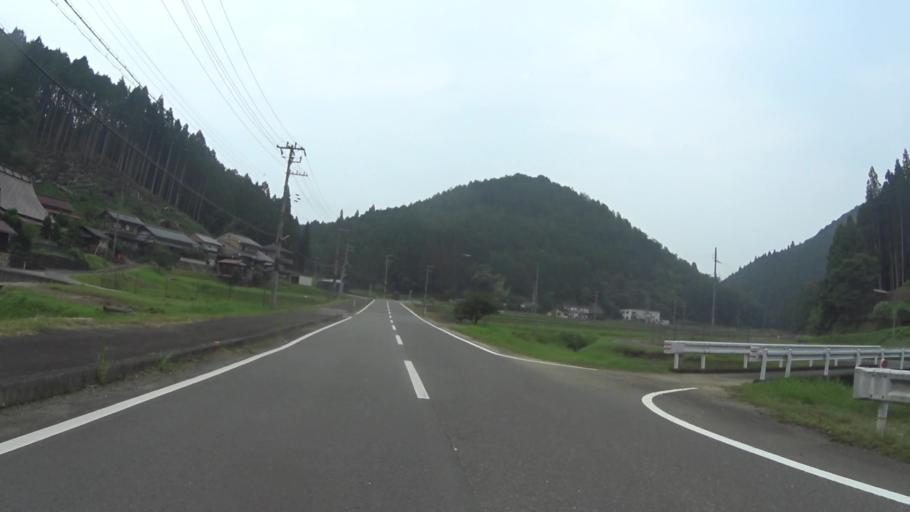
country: JP
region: Kyoto
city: Kameoka
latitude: 35.1587
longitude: 135.5999
